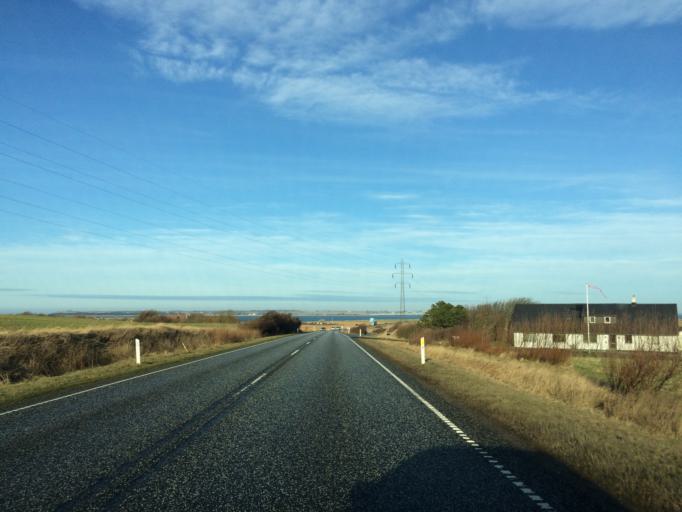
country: DK
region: Central Jutland
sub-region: Struer Kommune
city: Struer
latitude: 56.5557
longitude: 8.5577
